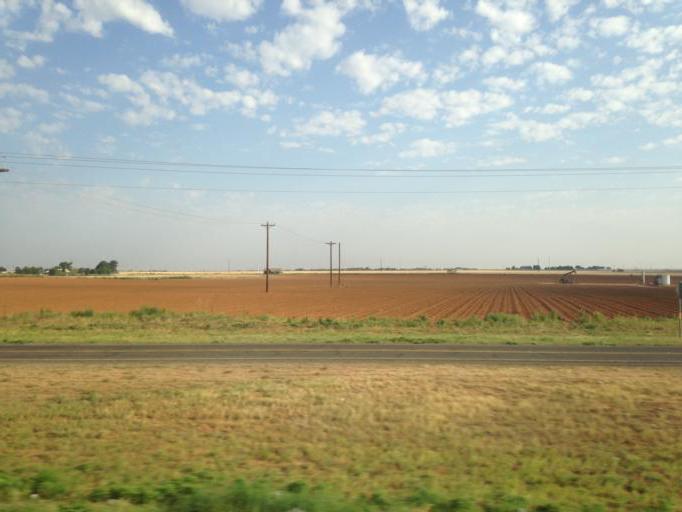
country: US
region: Texas
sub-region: Martin County
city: Stanton
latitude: 32.1128
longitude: -101.8355
